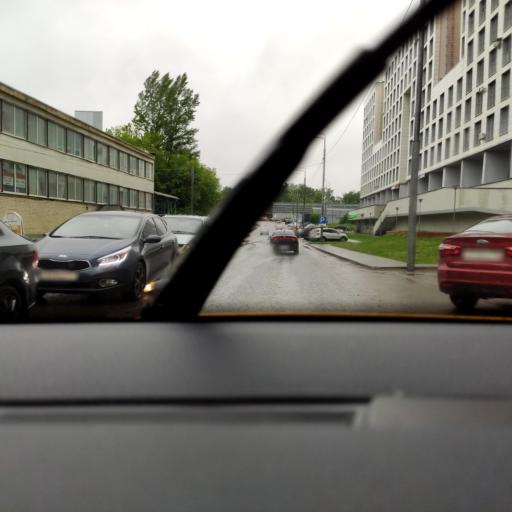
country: RU
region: Moskovskaya
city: Balashikha
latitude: 55.7986
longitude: 37.9645
